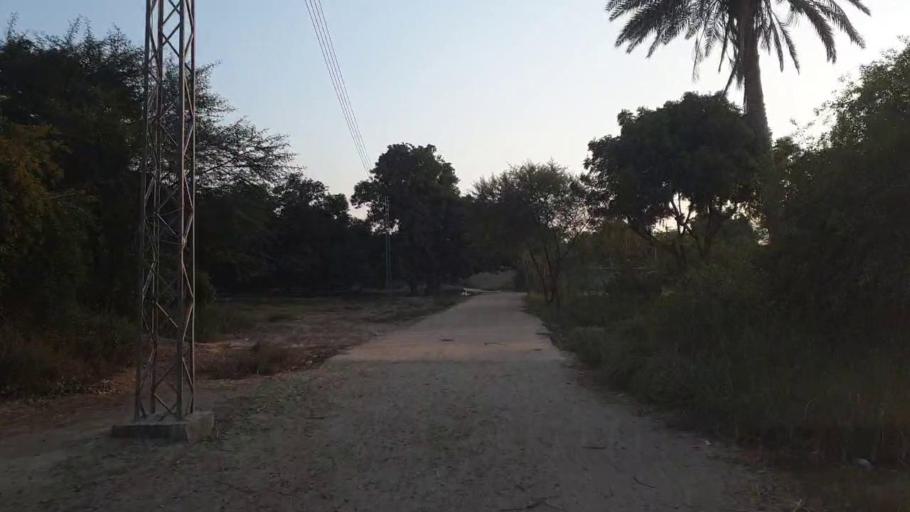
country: PK
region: Sindh
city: Chambar
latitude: 25.4159
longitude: 68.8790
